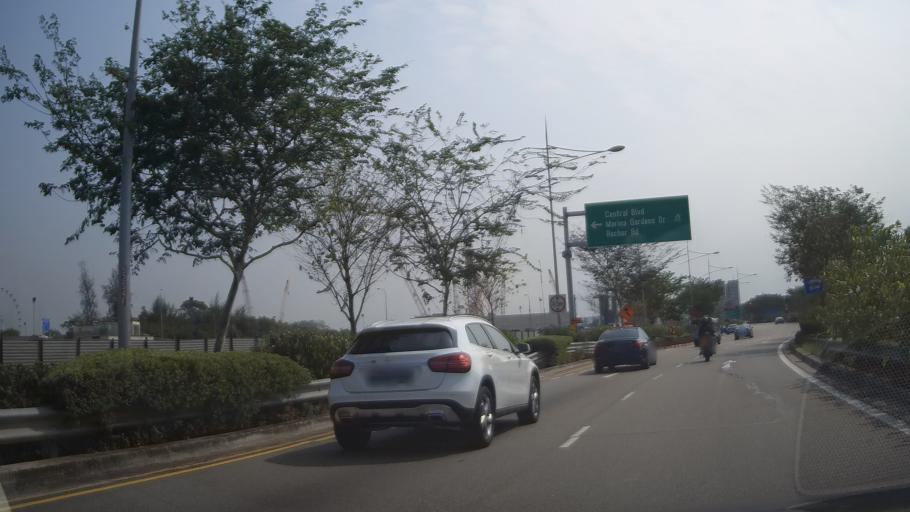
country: SG
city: Singapore
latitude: 1.2718
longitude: 103.8615
